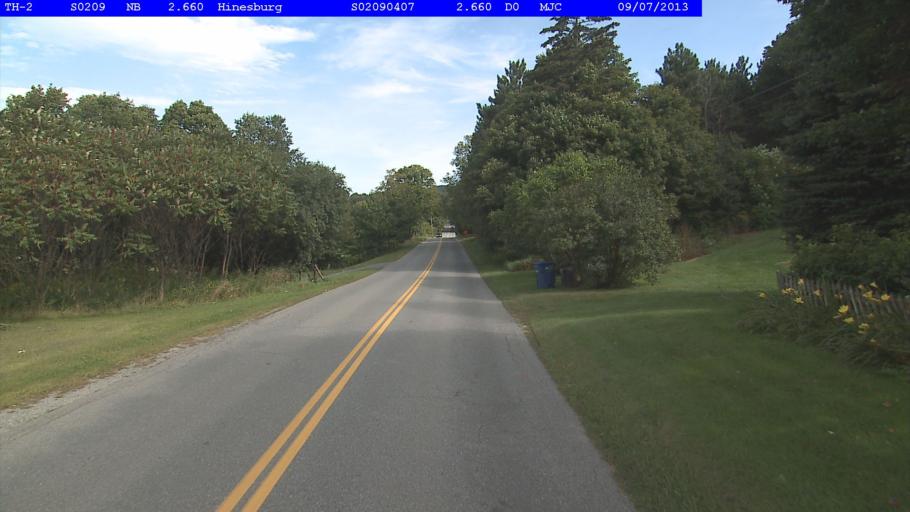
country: US
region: Vermont
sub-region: Chittenden County
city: Hinesburg
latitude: 44.3495
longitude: -73.0766
